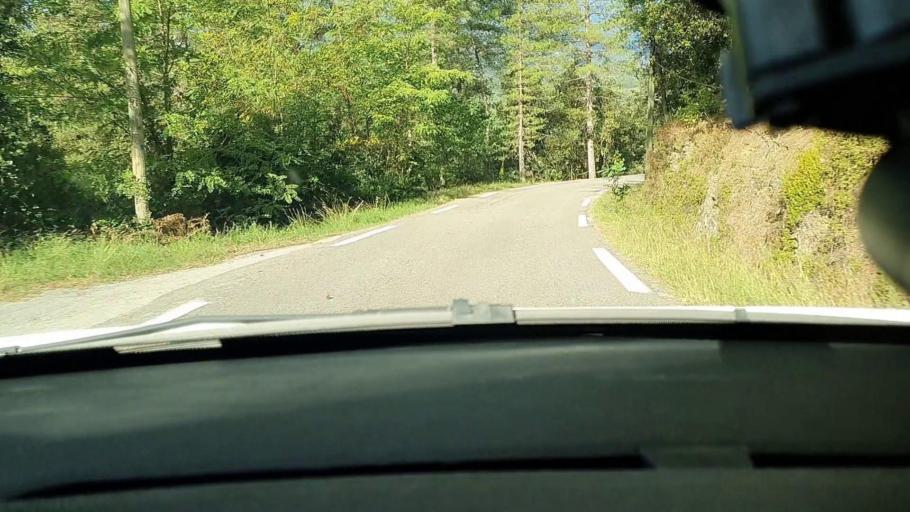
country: FR
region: Languedoc-Roussillon
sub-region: Departement du Gard
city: Besseges
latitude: 44.3632
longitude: 4.0013
